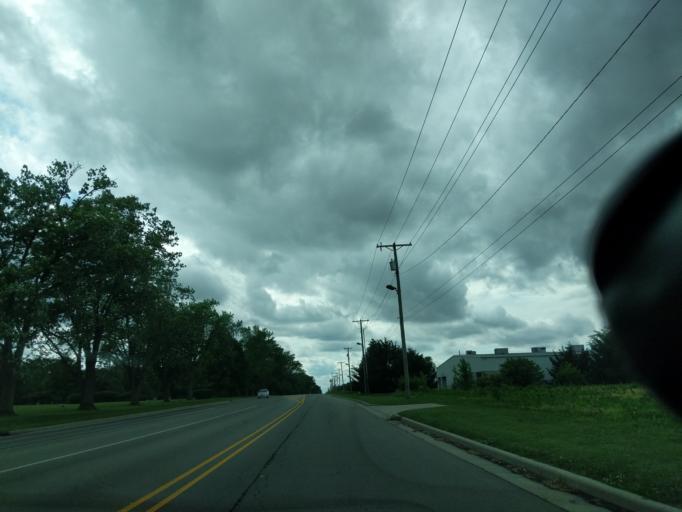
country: US
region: Indiana
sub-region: Madison County
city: Pendleton
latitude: 40.0469
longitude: -85.7200
